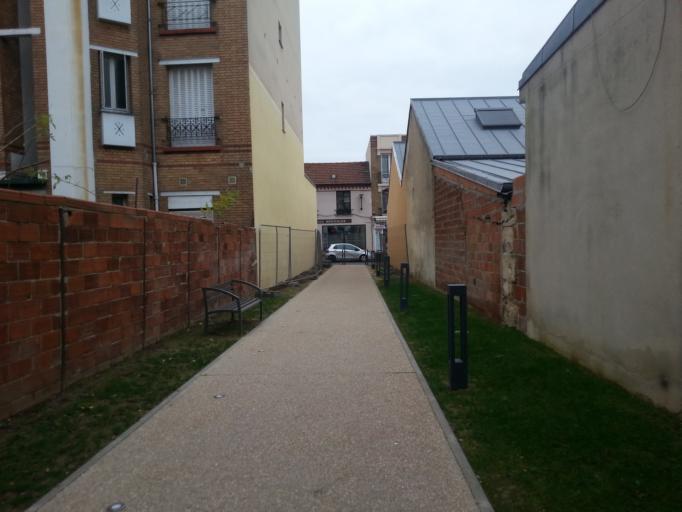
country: FR
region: Ile-de-France
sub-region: Departement des Yvelines
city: Houilles
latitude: 48.9238
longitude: 2.1874
